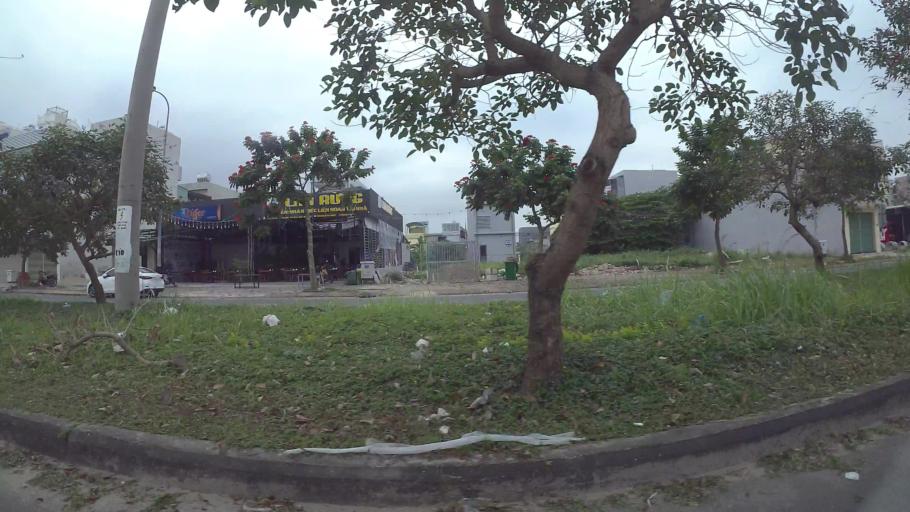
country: VN
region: Da Nang
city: Lien Chieu
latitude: 16.0605
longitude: 108.1717
